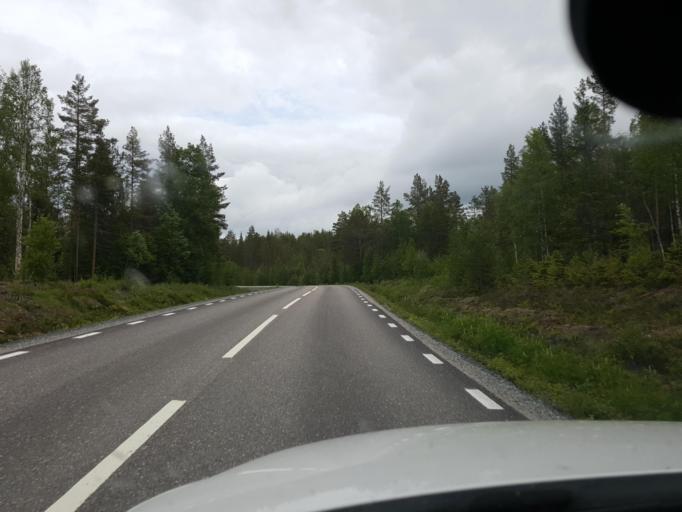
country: SE
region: Gaevleborg
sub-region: Ljusdals Kommun
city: Farila
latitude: 61.7519
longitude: 15.3727
